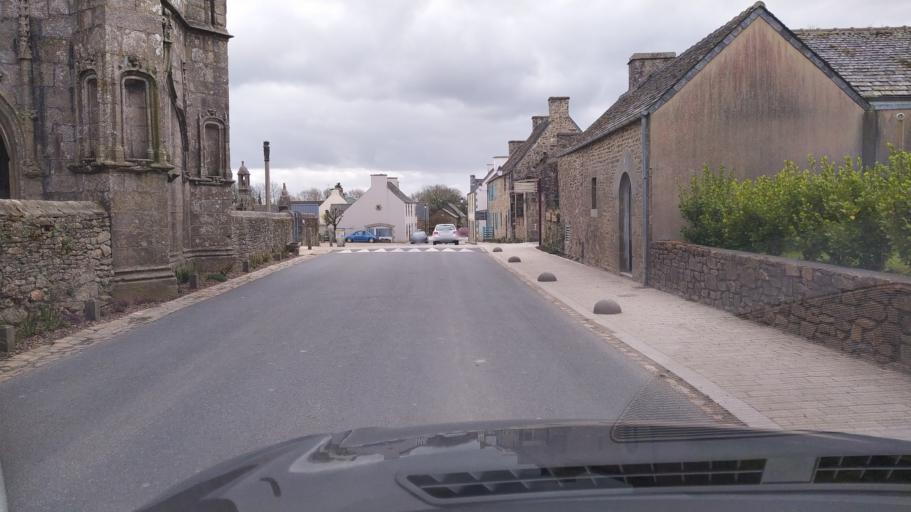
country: FR
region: Brittany
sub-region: Departement du Finistere
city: Bodilis
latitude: 48.5308
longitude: -4.1165
